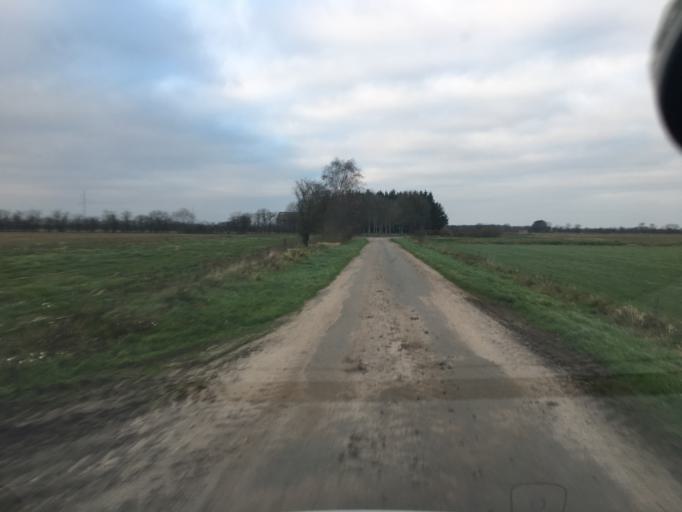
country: DK
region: South Denmark
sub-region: Tonder Kommune
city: Logumkloster
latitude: 55.0525
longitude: 9.0478
